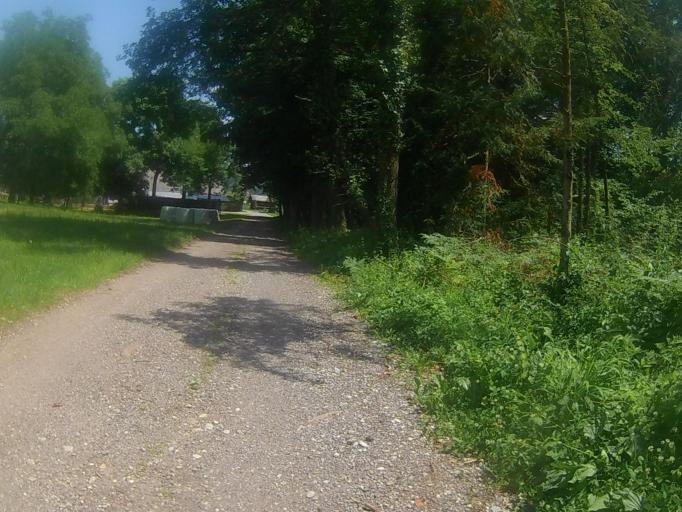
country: SI
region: Ruse
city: Bistrica ob Dravi
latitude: 46.5554
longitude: 15.5389
